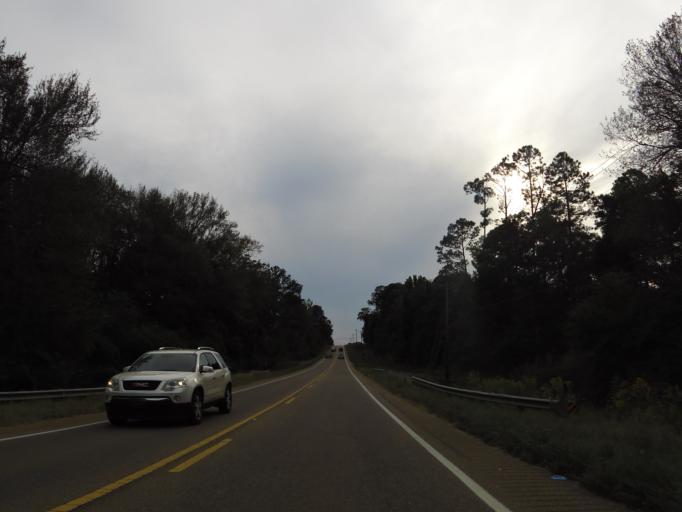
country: US
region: Alabama
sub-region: Monroe County
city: Frisco City
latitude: 31.4528
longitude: -87.3727
